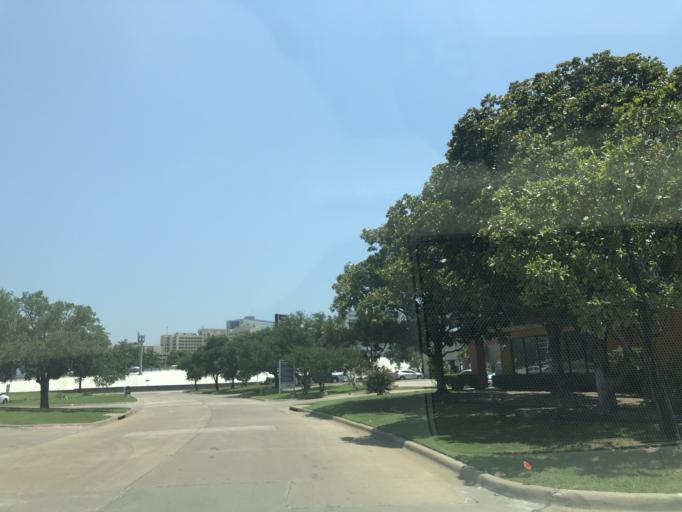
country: US
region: Texas
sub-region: Dallas County
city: Dallas
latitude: 32.8062
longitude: -96.8433
